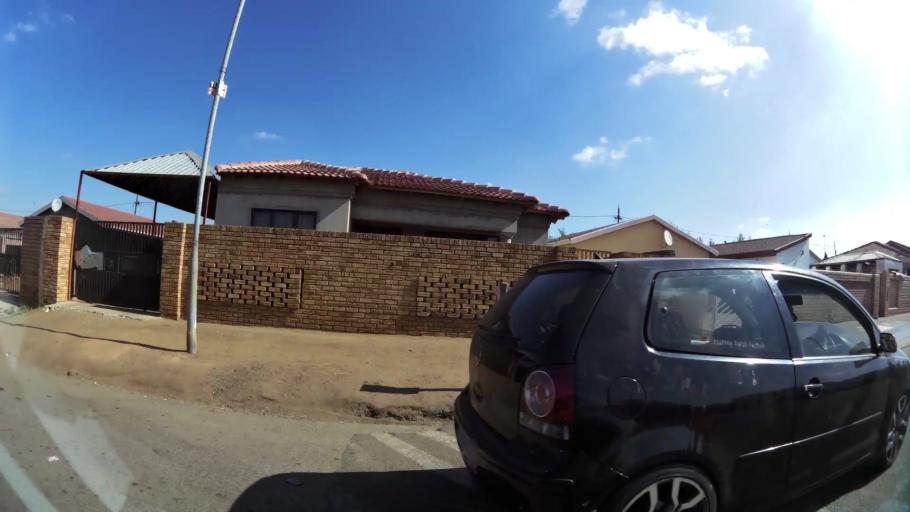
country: ZA
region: Gauteng
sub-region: City of Johannesburg Metropolitan Municipality
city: Soweto
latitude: -26.2556
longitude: 27.8883
